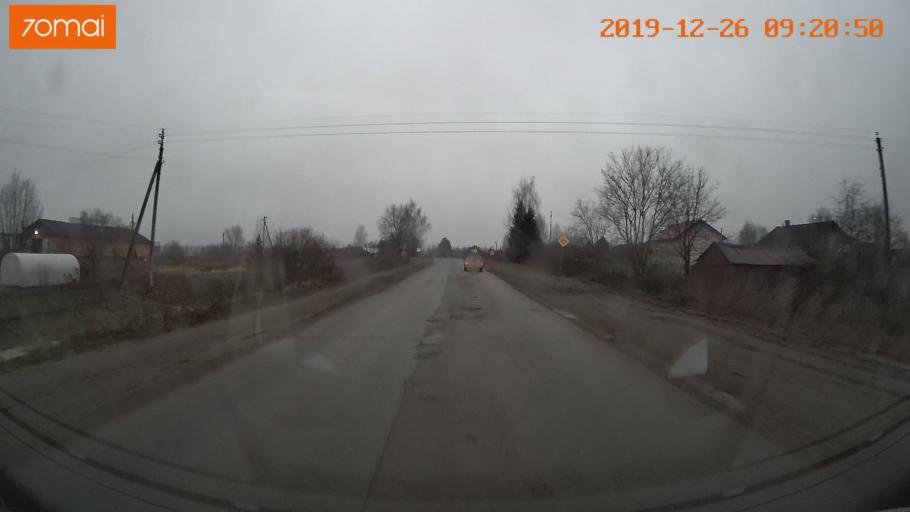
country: RU
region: Vologda
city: Gryazovets
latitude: 58.9648
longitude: 40.2275
